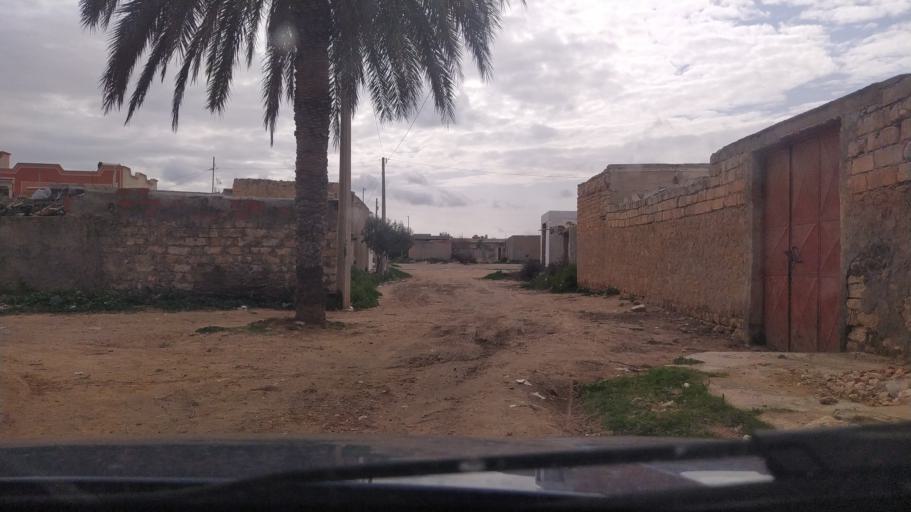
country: TN
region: Al Munastir
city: Sidi Bin Nur
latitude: 35.5183
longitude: 10.9289
